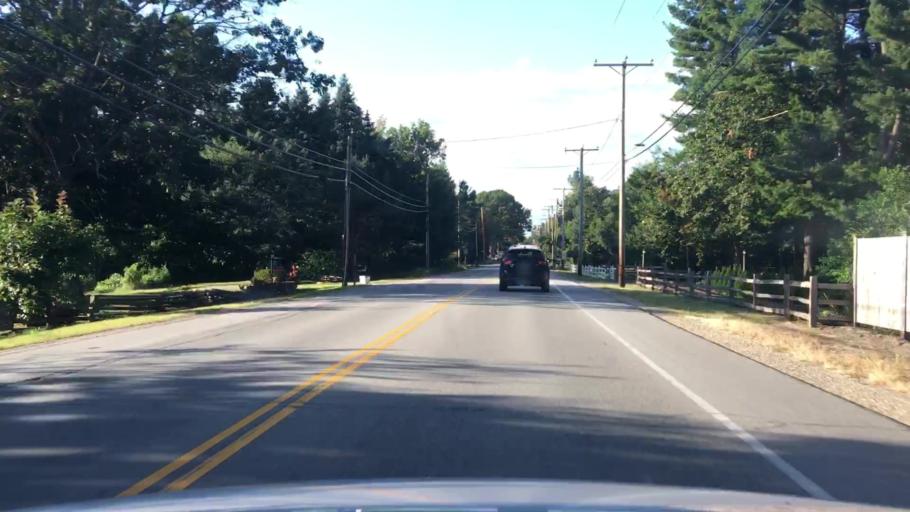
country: US
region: Maine
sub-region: York County
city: Eliot
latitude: 43.1471
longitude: -70.8390
